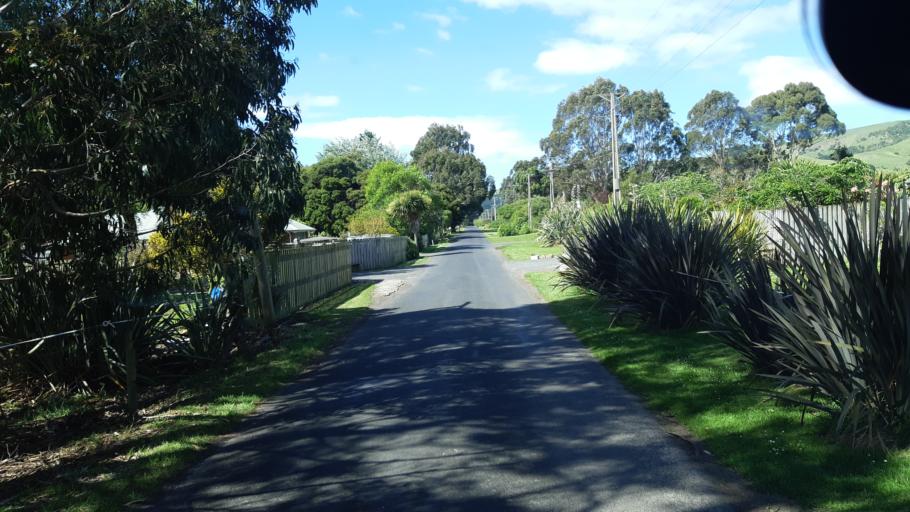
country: NZ
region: Otago
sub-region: Dunedin City
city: Portobello
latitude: -45.8158
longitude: 170.6740
